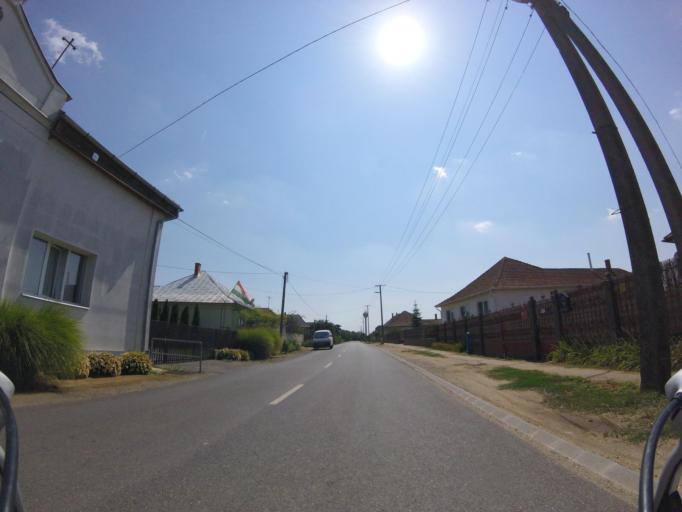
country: HU
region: Szabolcs-Szatmar-Bereg
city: Nyirmeggyes
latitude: 47.9846
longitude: 22.2500
